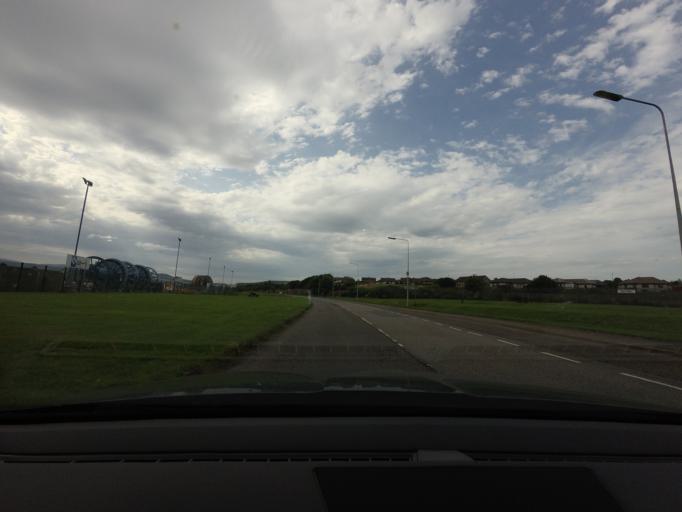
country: GB
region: Scotland
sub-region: Highland
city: Invergordon
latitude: 57.6881
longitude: -4.1772
